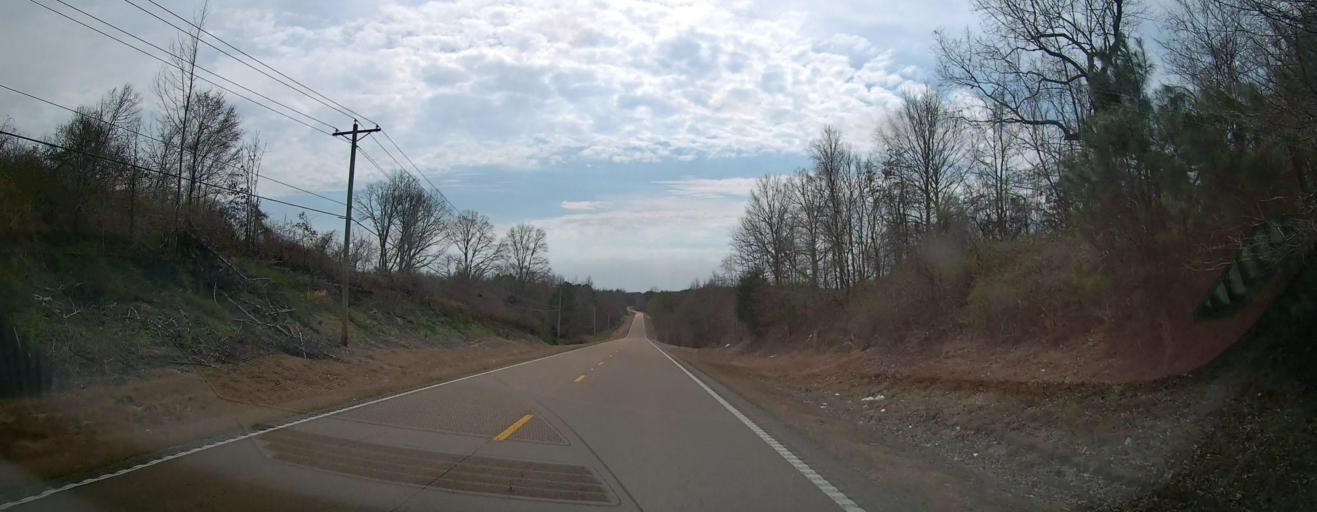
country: US
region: Mississippi
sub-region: Marshall County
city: Holly Springs
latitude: 34.7346
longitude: -89.4220
